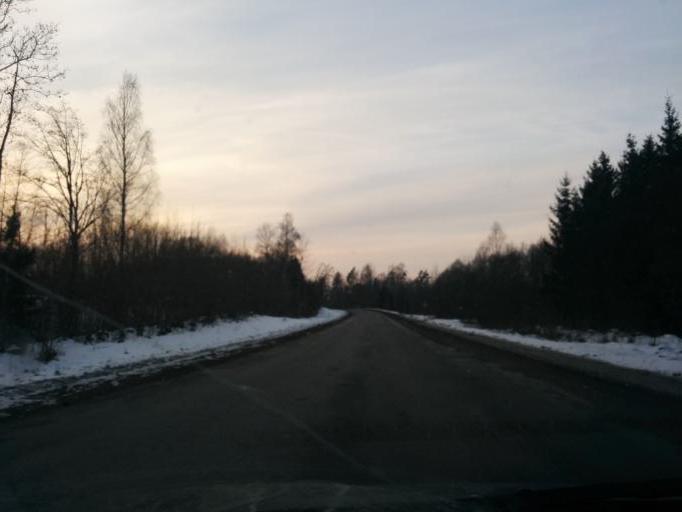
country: LV
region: Priekuli
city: Priekuli
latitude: 57.2700
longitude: 25.4554
